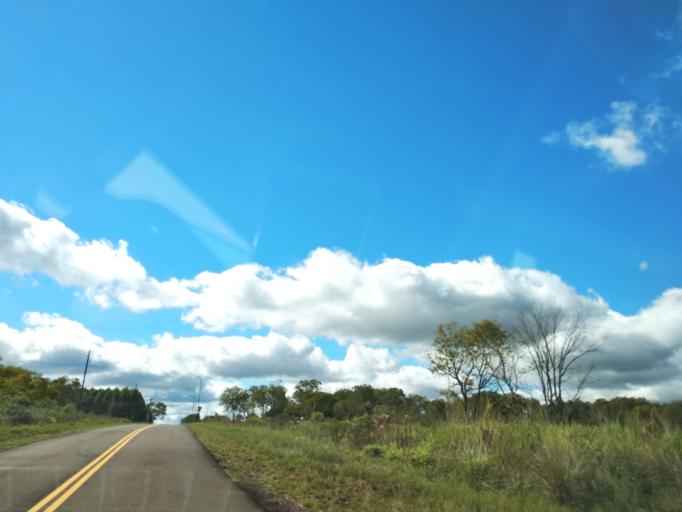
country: AR
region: Misiones
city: Santa Ana
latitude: -27.4094
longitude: -55.5549
